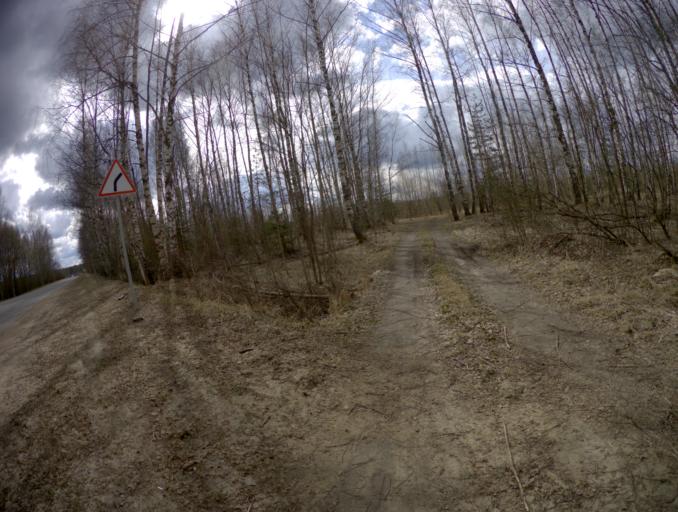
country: RU
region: Vladimir
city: Raduzhnyy
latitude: 55.9651
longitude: 40.2468
